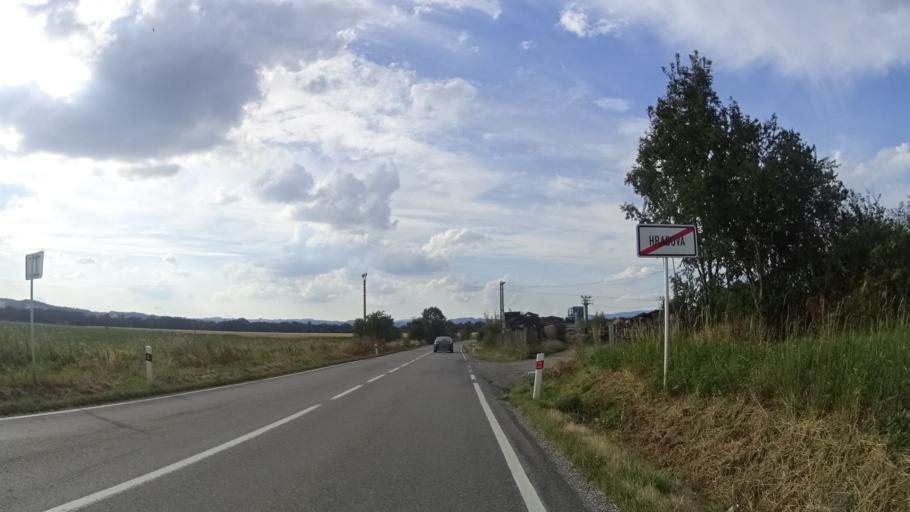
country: CZ
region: Olomoucky
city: Dubicko
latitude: 49.8468
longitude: 16.9491
